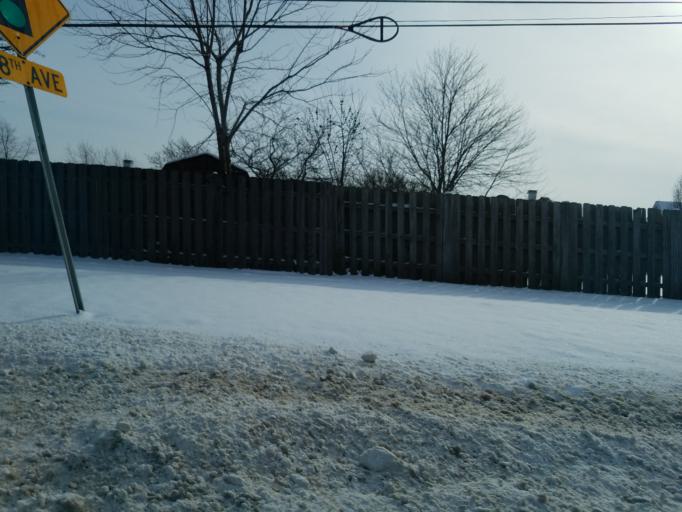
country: US
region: Illinois
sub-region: Cook County
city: Orland Park
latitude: 41.6162
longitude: -87.8375
